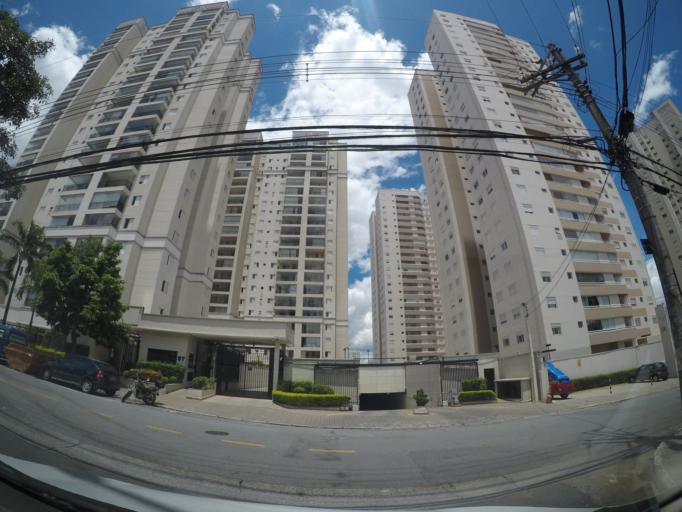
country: BR
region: Sao Paulo
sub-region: Guarulhos
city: Guarulhos
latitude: -23.4637
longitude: -46.5344
